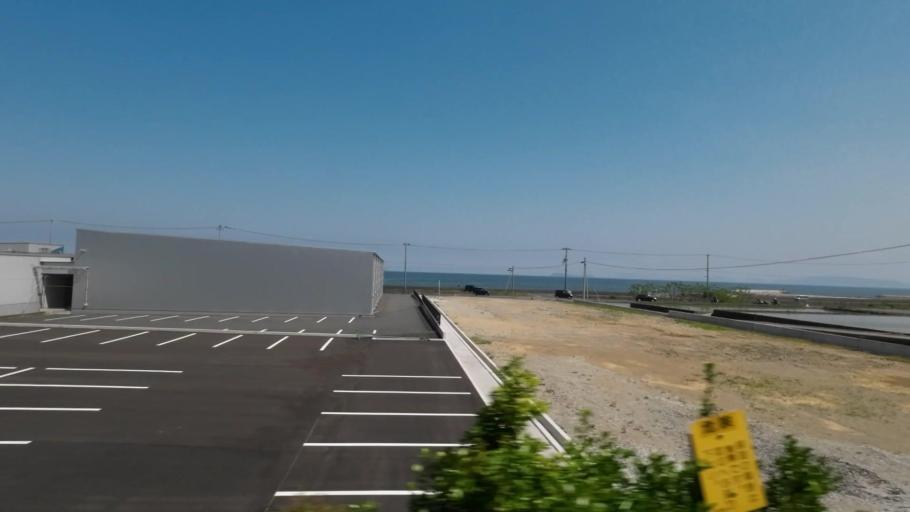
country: JP
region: Ehime
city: Kawanoecho
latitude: 33.9677
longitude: 133.4928
